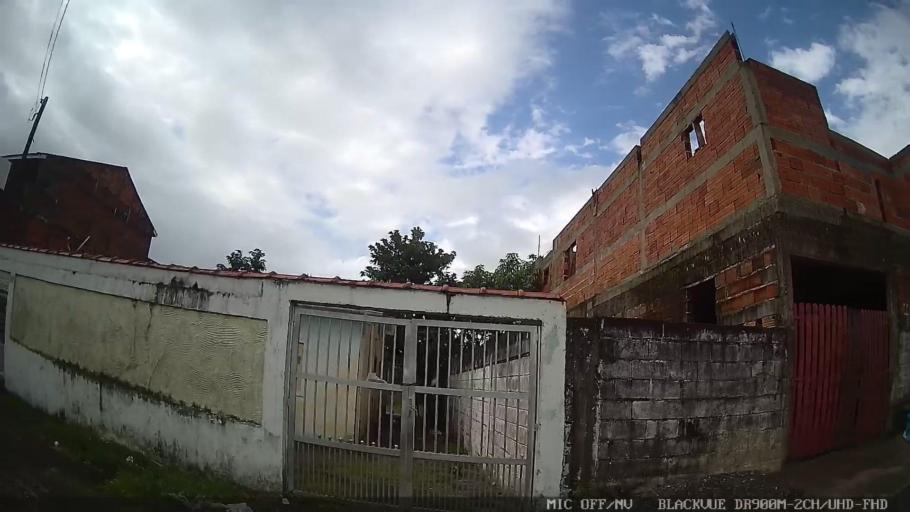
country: BR
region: Sao Paulo
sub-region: Itanhaem
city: Itanhaem
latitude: -24.1862
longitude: -46.8128
